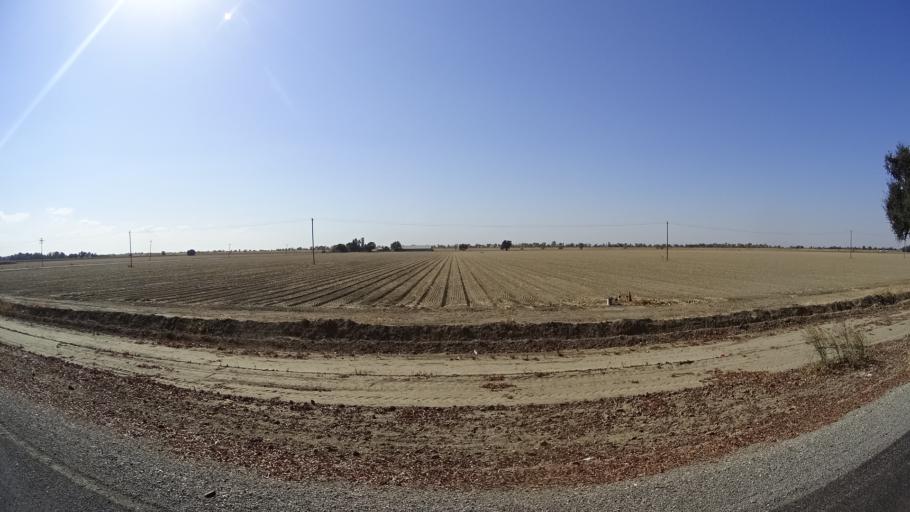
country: US
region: California
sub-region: Yolo County
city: West Sacramento
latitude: 38.6686
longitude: -121.6227
